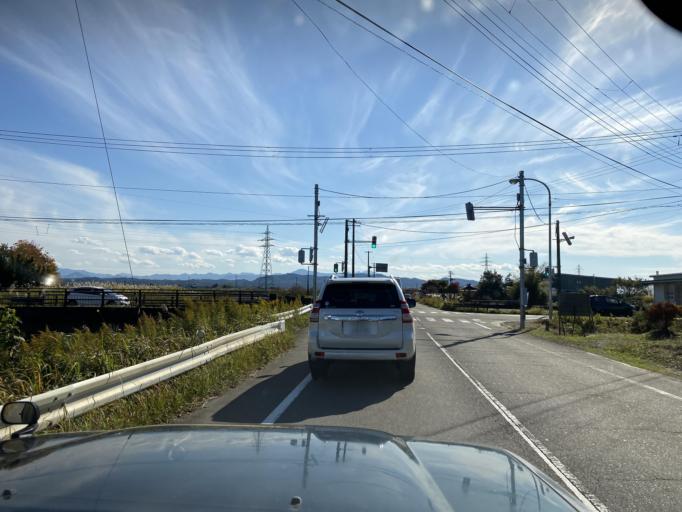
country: JP
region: Niigata
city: Niitsu-honcho
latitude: 37.7913
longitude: 139.0801
